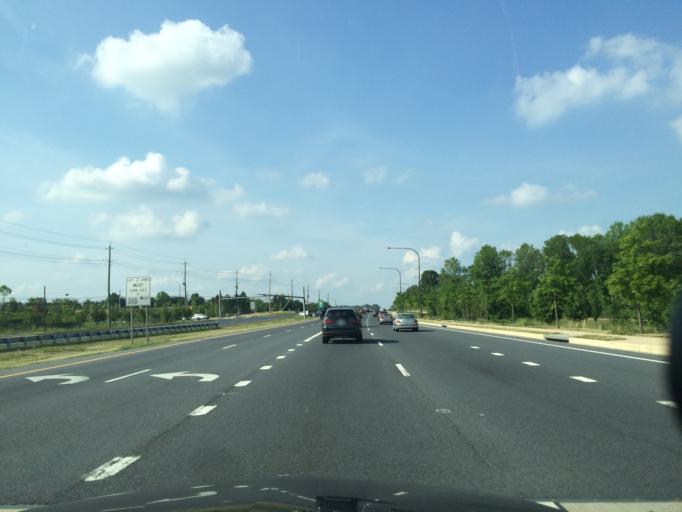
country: US
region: Maryland
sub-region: Montgomery County
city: Rossmoor
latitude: 39.1184
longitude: -77.0747
